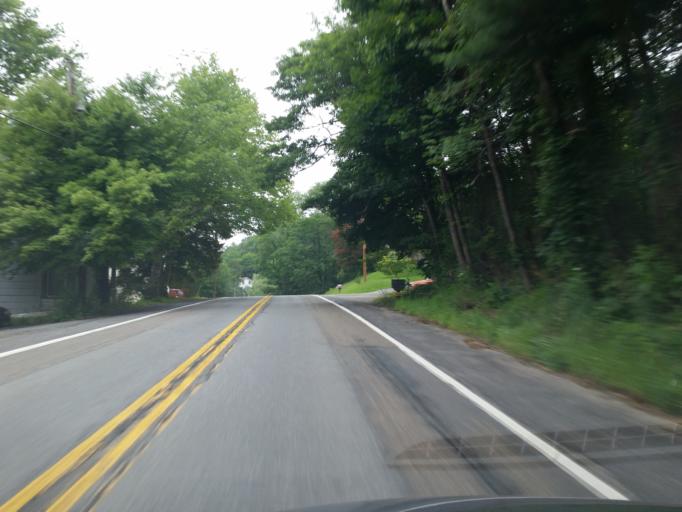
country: US
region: Pennsylvania
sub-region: Schuylkill County
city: Pine Grove
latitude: 40.5288
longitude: -76.4580
